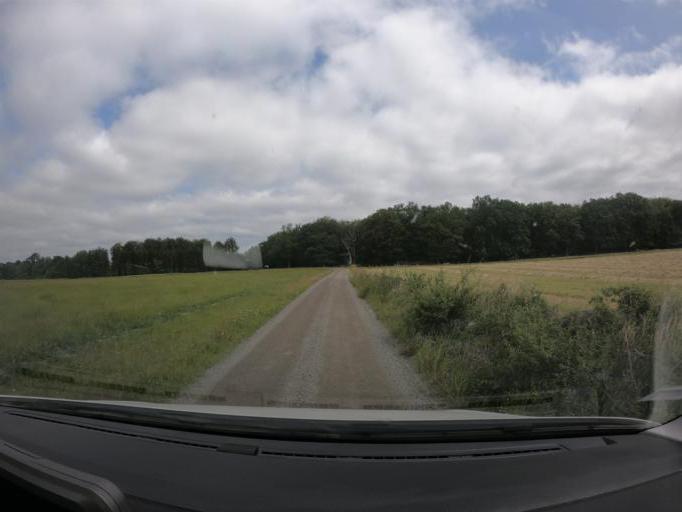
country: SE
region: Skane
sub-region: Hassleholms Kommun
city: Sosdala
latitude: 56.0675
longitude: 13.6662
